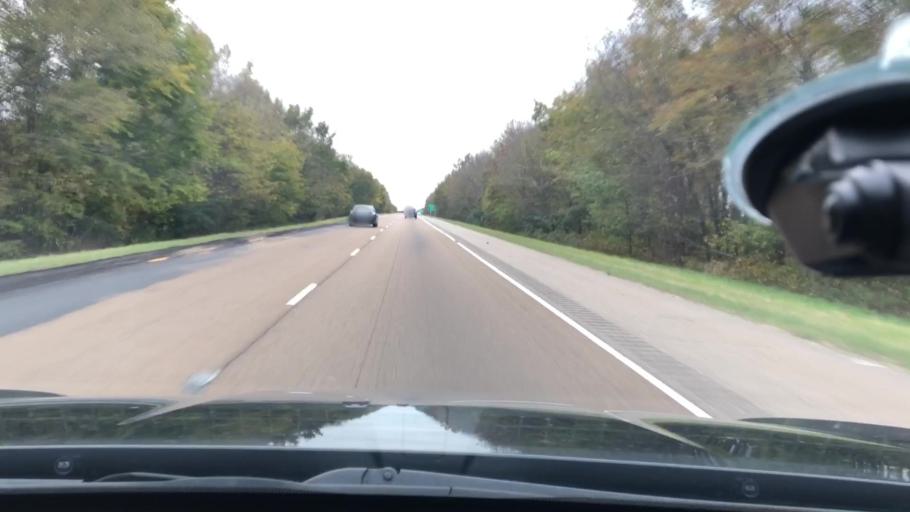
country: US
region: Arkansas
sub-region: Nevada County
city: Prescott
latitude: 33.8039
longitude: -93.4322
